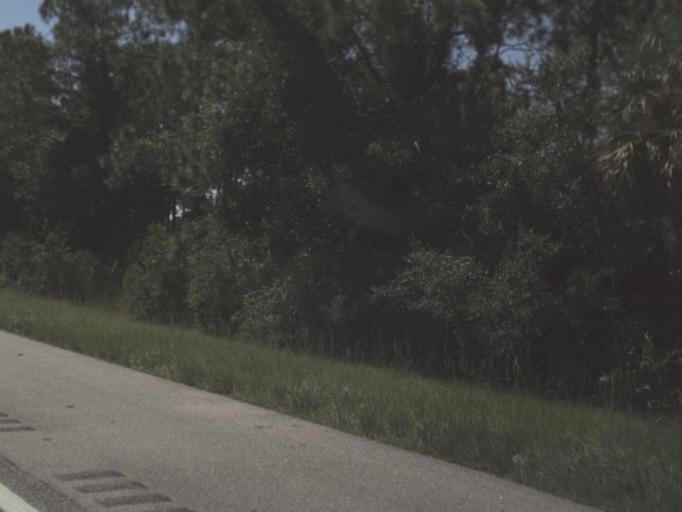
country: US
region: Florida
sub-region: Lee County
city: Suncoast Estates
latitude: 26.8072
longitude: -81.9282
